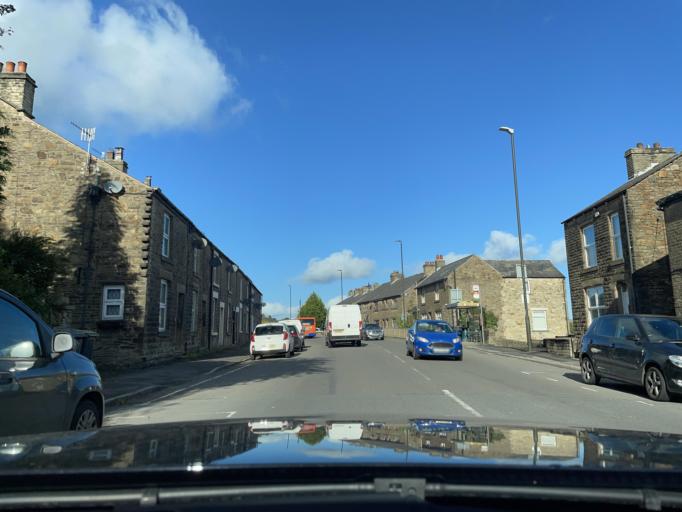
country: GB
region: England
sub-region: Derbyshire
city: New Mills
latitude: 53.3493
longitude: -1.9911
